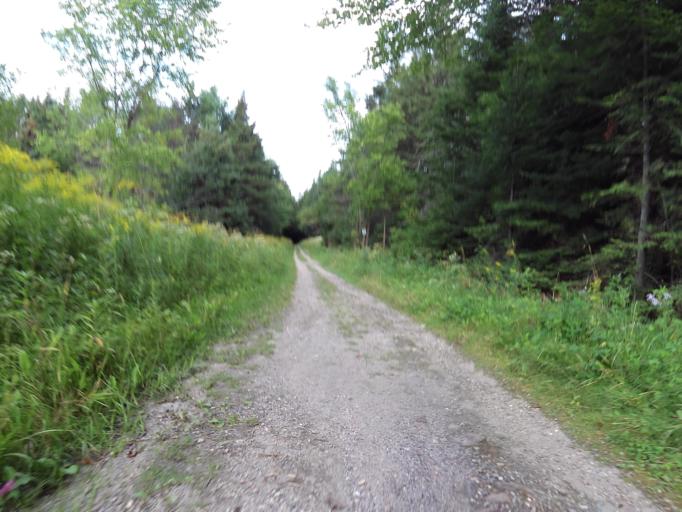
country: CA
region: Quebec
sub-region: Outaouais
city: Wakefield
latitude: 45.6317
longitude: -75.9454
